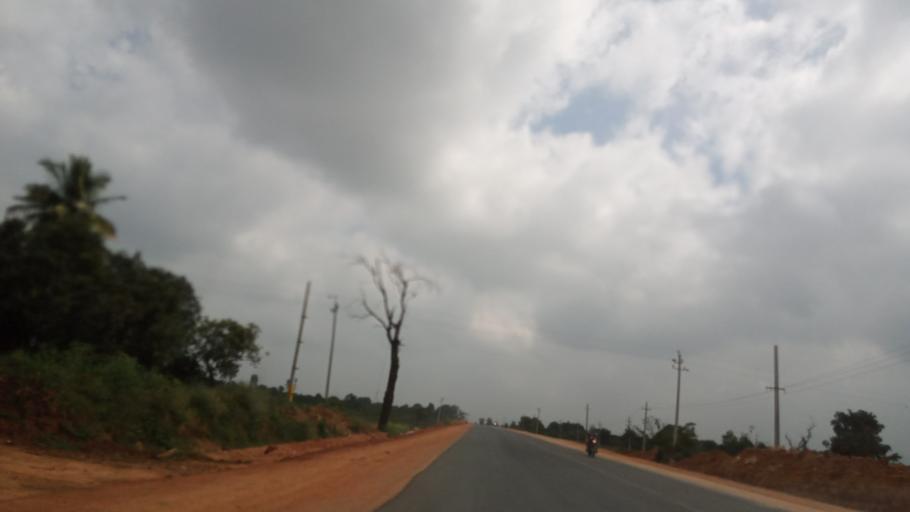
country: IN
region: Karnataka
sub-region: Kolar
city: Srinivaspur
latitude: 13.4460
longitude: 78.2383
